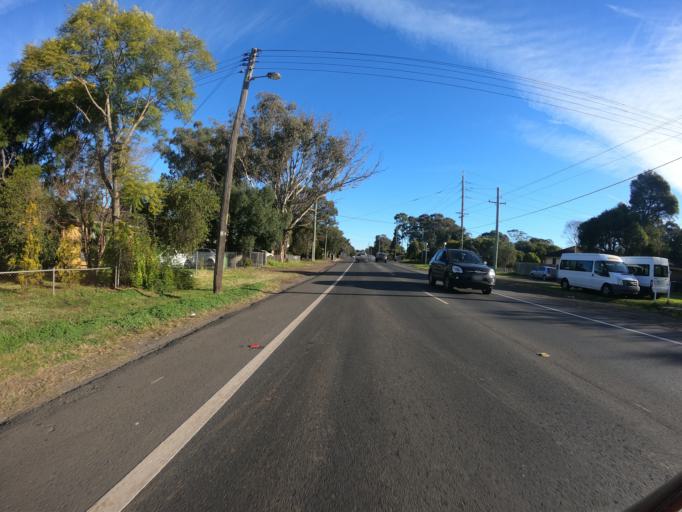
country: AU
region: New South Wales
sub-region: Hawkesbury
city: South Windsor
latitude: -33.6283
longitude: 150.7956
